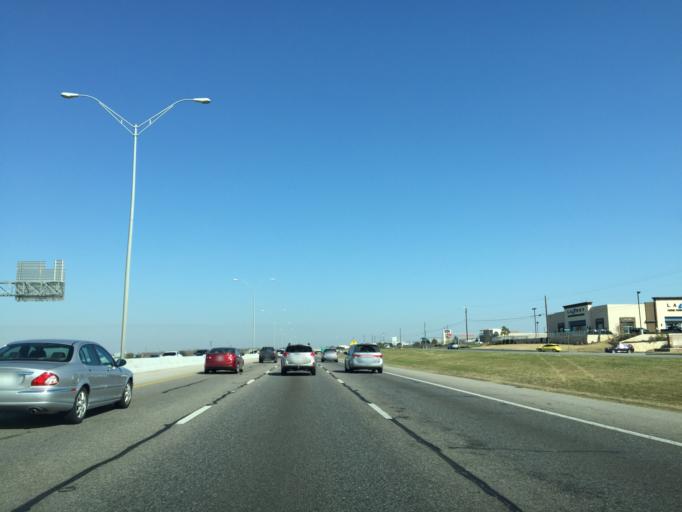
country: US
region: Texas
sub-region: Williamson County
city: Round Rock
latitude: 30.5677
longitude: -97.6925
